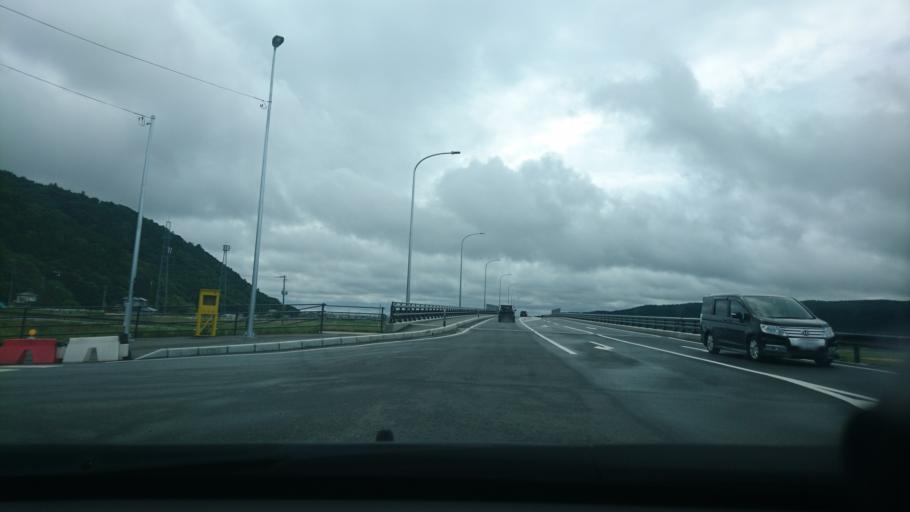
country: JP
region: Miyagi
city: Ishinomaki
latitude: 38.4479
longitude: 141.3499
